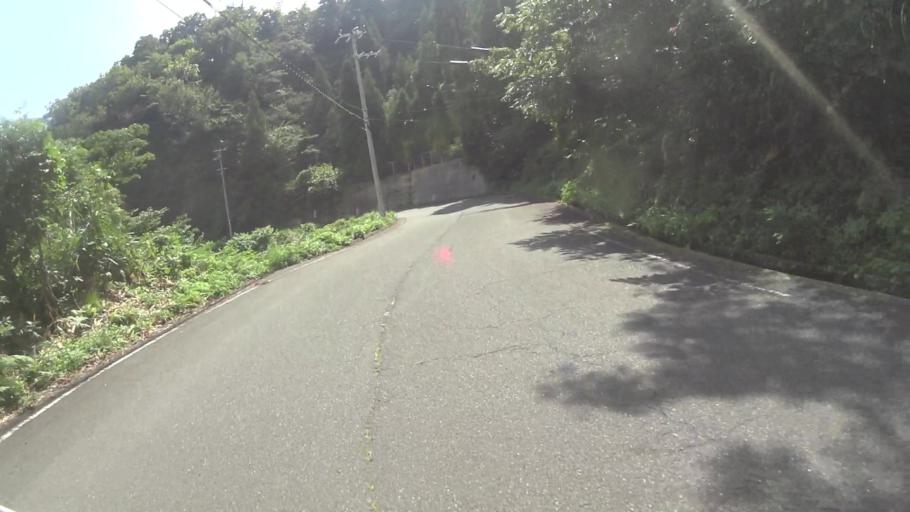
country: JP
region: Kyoto
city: Miyazu
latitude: 35.7167
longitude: 135.1942
